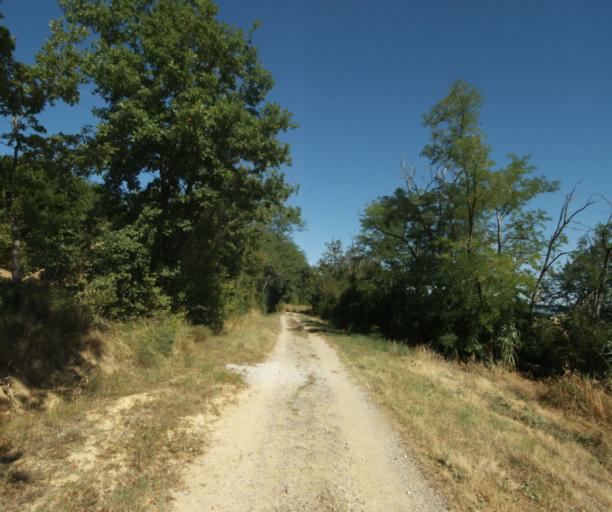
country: FR
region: Midi-Pyrenees
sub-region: Departement de la Haute-Garonne
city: Saint-Felix-Lauragais
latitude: 43.5157
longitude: 1.9200
